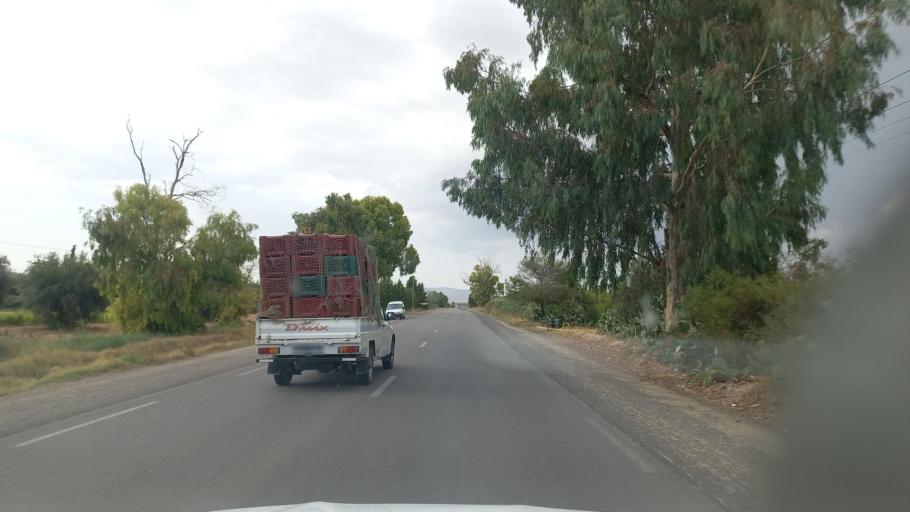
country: TN
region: Al Qasrayn
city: Sbiba
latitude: 35.2976
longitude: 9.0893
